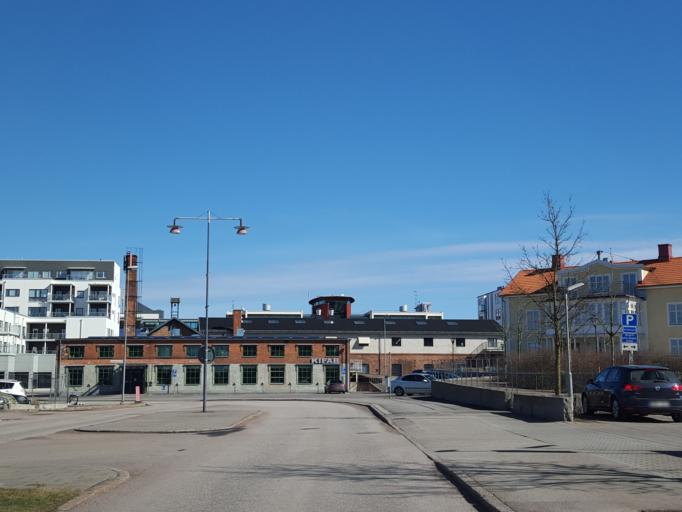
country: SE
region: Kalmar
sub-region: Kalmar Kommun
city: Kalmar
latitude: 56.6693
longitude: 16.3743
